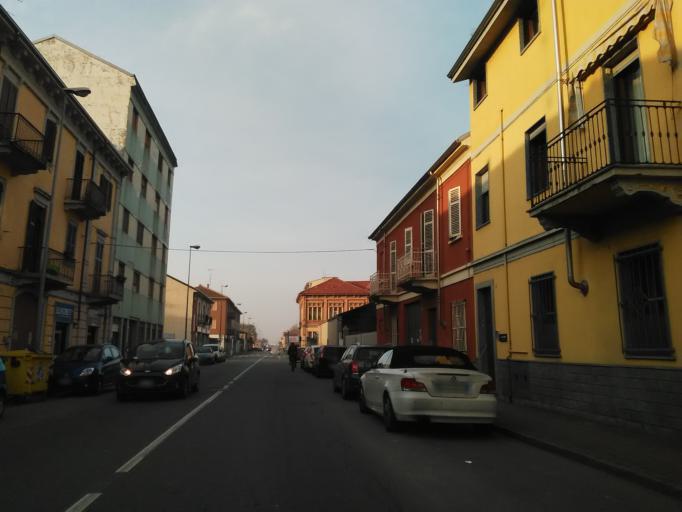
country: IT
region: Piedmont
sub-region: Provincia di Vercelli
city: Vercelli
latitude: 45.3312
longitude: 8.4101
